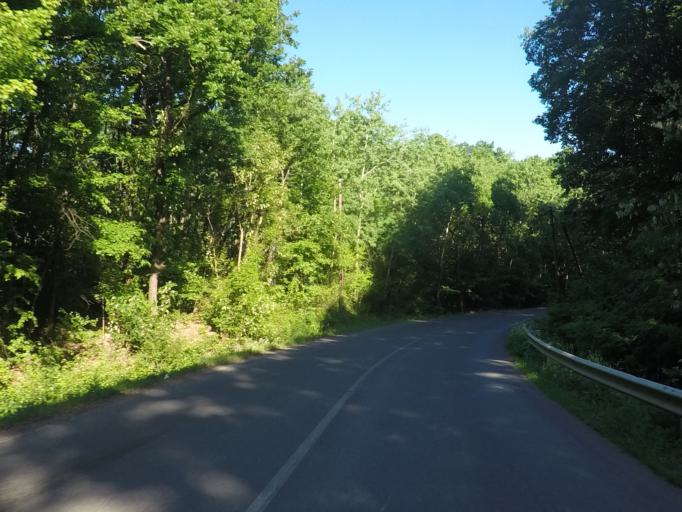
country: HU
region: Borsod-Abauj-Zemplen
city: Putnok
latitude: 48.4470
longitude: 20.4818
